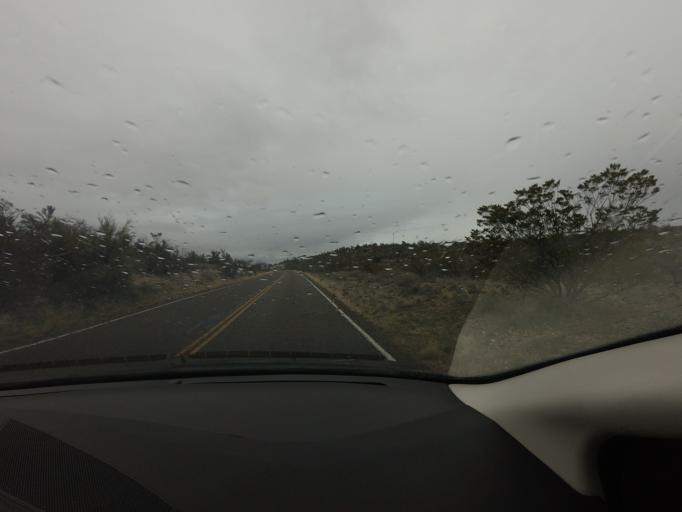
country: US
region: Arizona
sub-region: Yavapai County
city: Camp Verde
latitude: 34.6144
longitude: -111.8458
